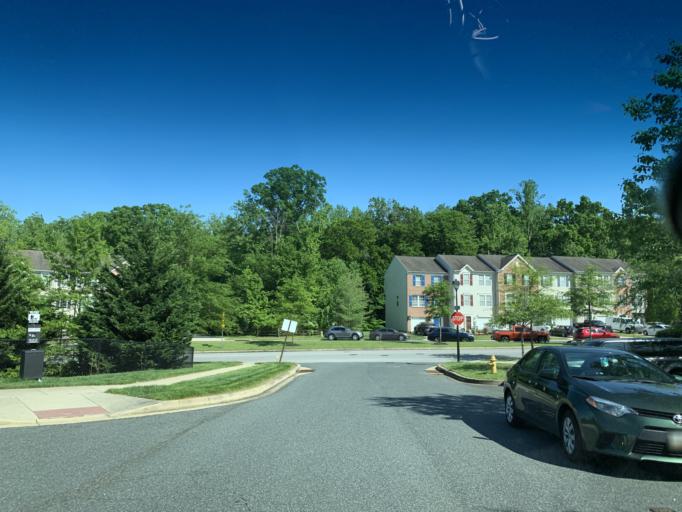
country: US
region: Maryland
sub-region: Harford County
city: Riverside
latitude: 39.4922
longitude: -76.2249
